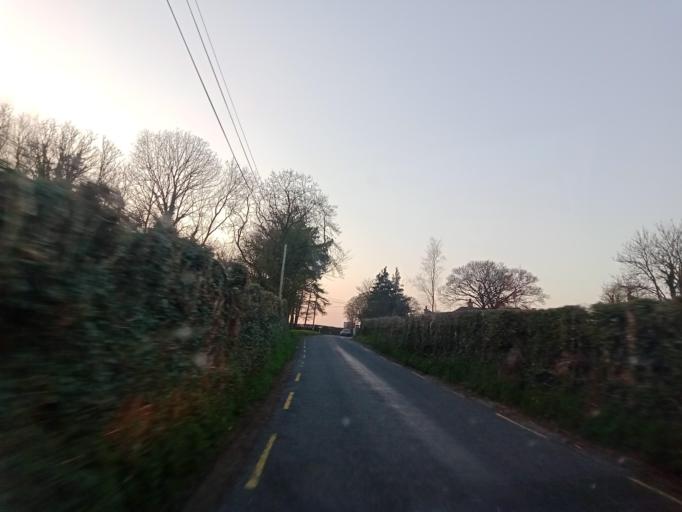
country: IE
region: Leinster
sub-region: Laois
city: Abbeyleix
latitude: 52.9608
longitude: -7.3643
